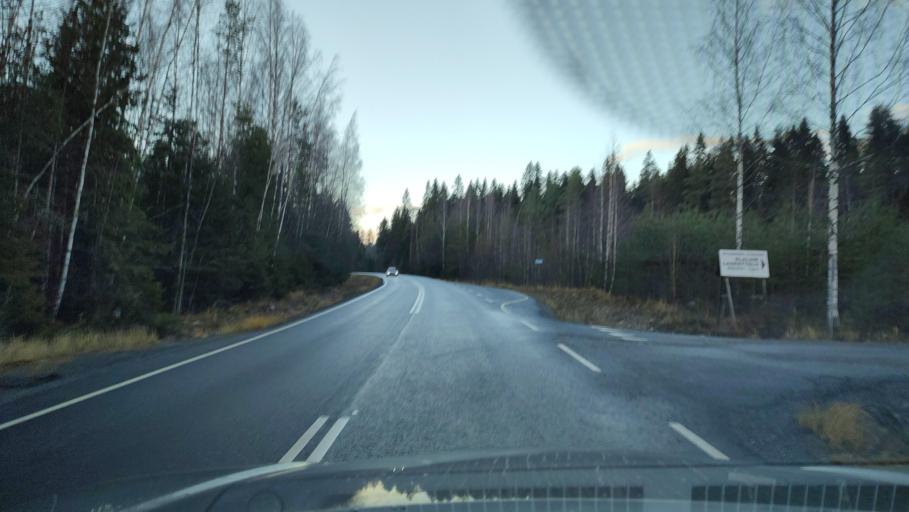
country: FI
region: Southern Ostrobothnia
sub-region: Suupohja
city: Karijoki
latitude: 62.2839
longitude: 21.6214
